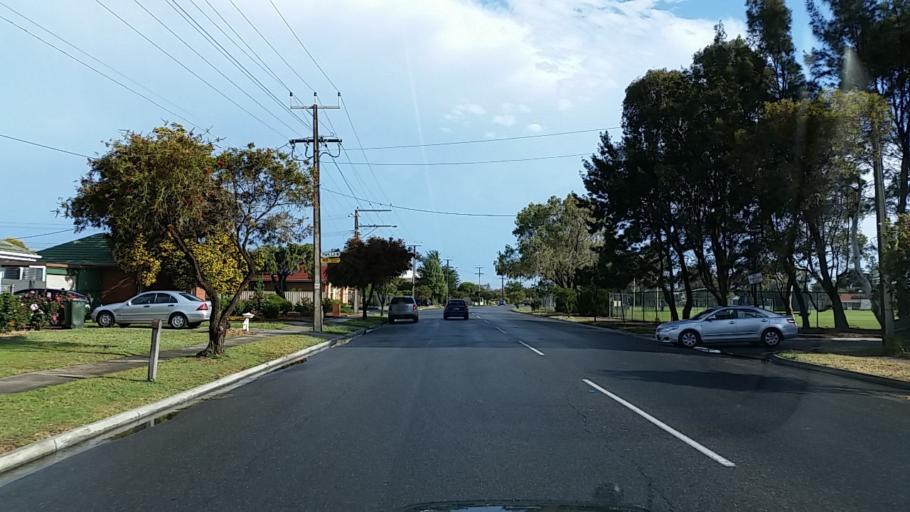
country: AU
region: South Australia
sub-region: Charles Sturt
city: Henley Beach
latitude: -34.9176
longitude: 138.5010
